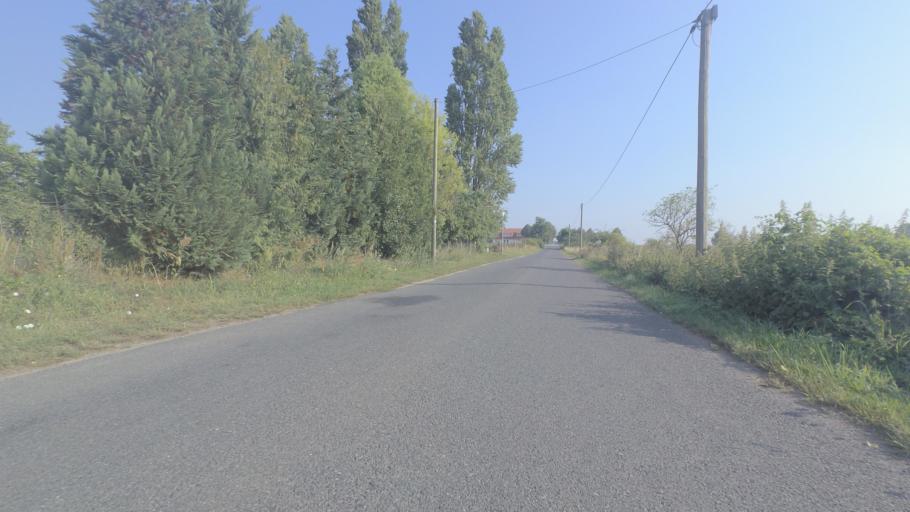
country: DE
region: Mecklenburg-Vorpommern
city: Malchow
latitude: 53.3640
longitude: 12.3821
